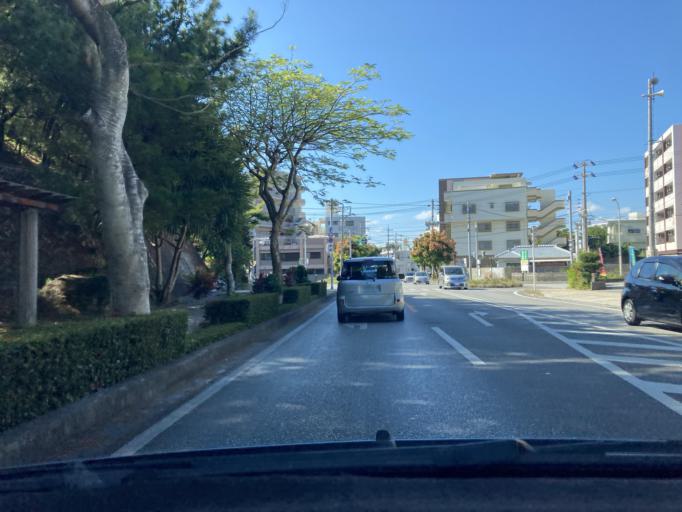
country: JP
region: Okinawa
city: Naha-shi
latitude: 26.2379
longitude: 127.6989
